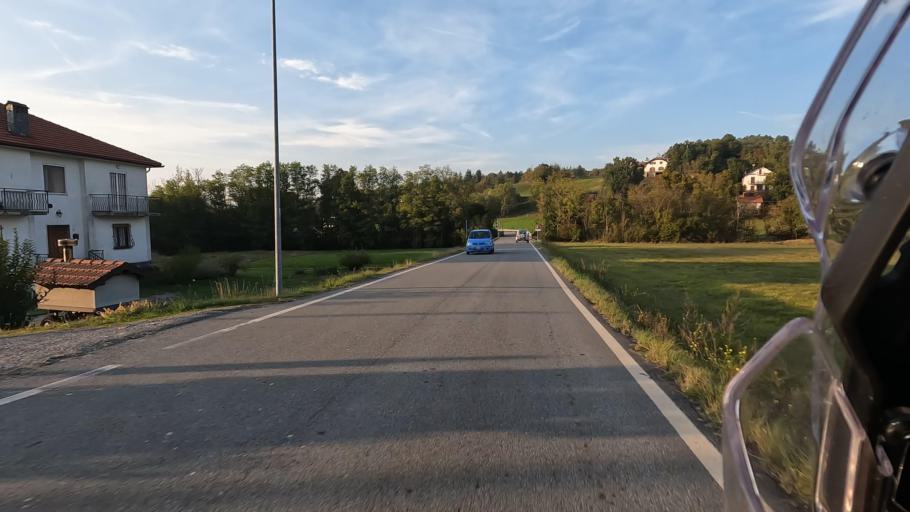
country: IT
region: Liguria
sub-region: Provincia di Savona
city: Sassello
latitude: 44.4964
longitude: 8.4962
